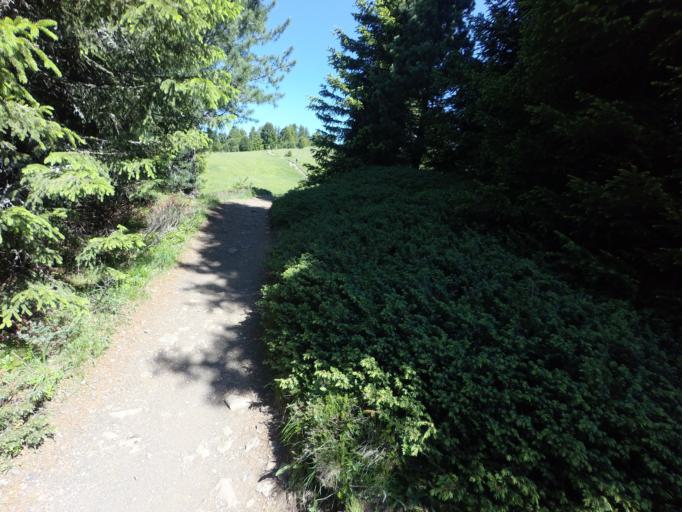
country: IT
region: Trentino-Alto Adige
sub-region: Bolzano
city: Castelrotto
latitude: 46.5550
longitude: 11.5996
